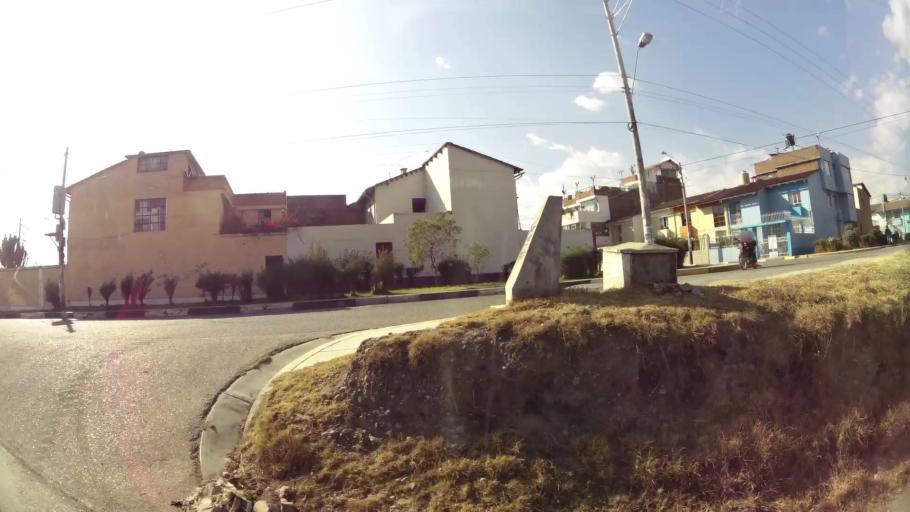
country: PE
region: Junin
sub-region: Provincia de Huancayo
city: El Tambo
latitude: -12.0640
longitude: -75.2251
